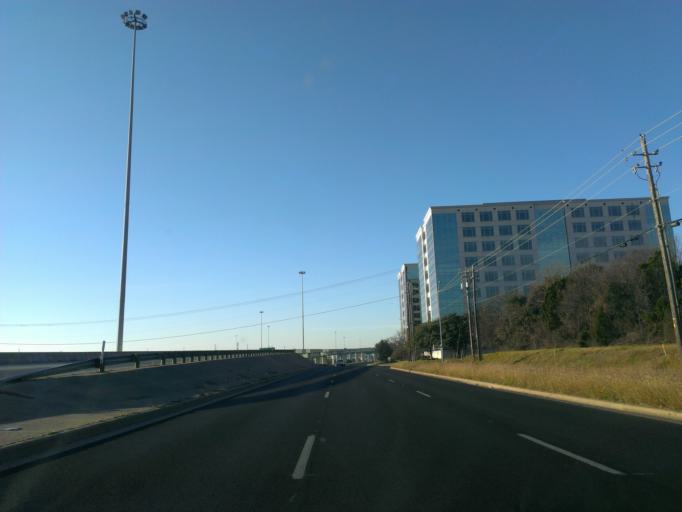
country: US
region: Texas
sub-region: Williamson County
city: Jollyville
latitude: 30.3875
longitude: -97.7355
